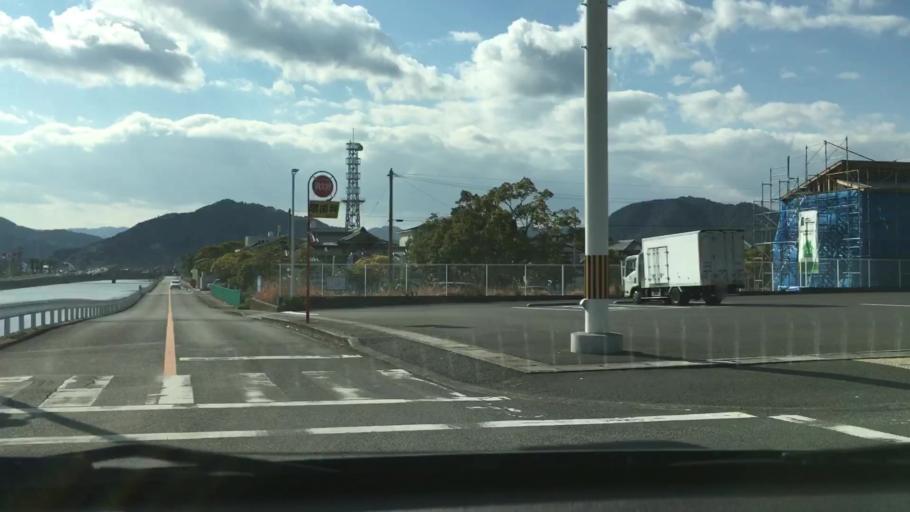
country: JP
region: Oita
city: Saiki
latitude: 32.9562
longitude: 131.9088
